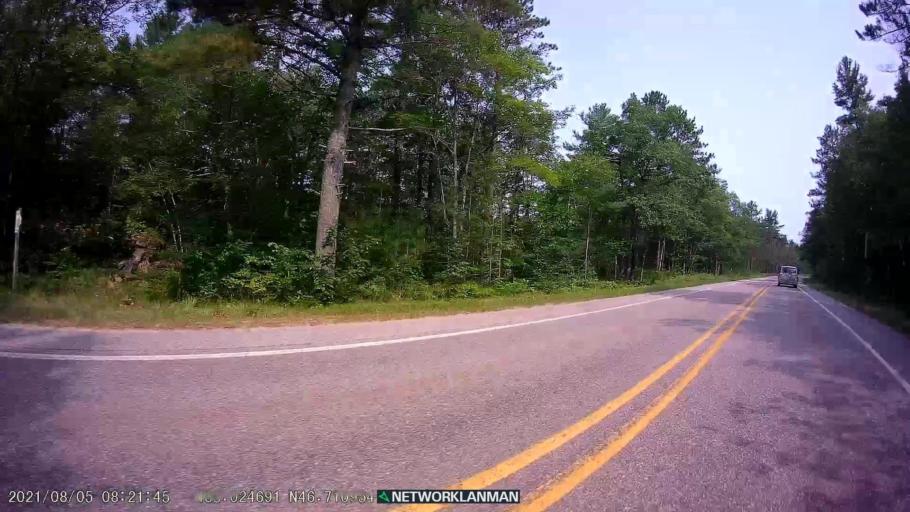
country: US
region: Michigan
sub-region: Luce County
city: Newberry
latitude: 46.7115
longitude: -85.0245
